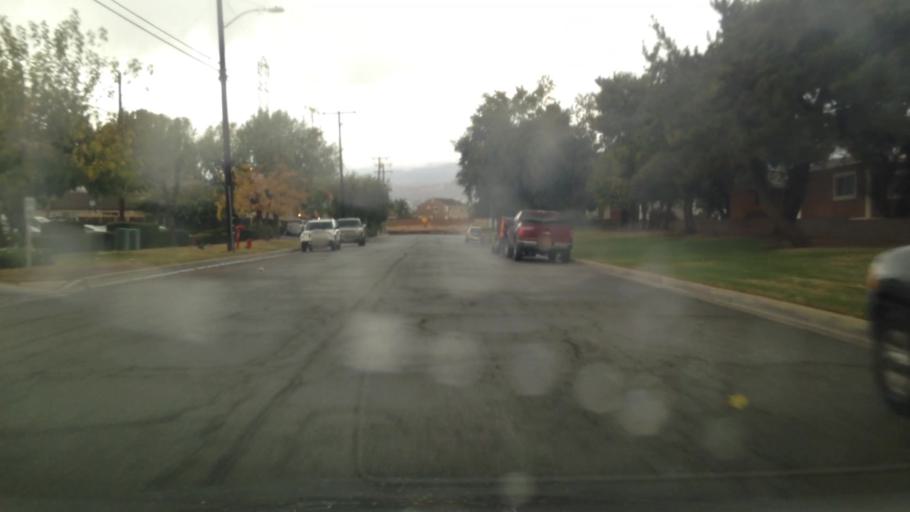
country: US
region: California
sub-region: Riverside County
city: Beaumont
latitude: 33.9479
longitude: -116.9689
